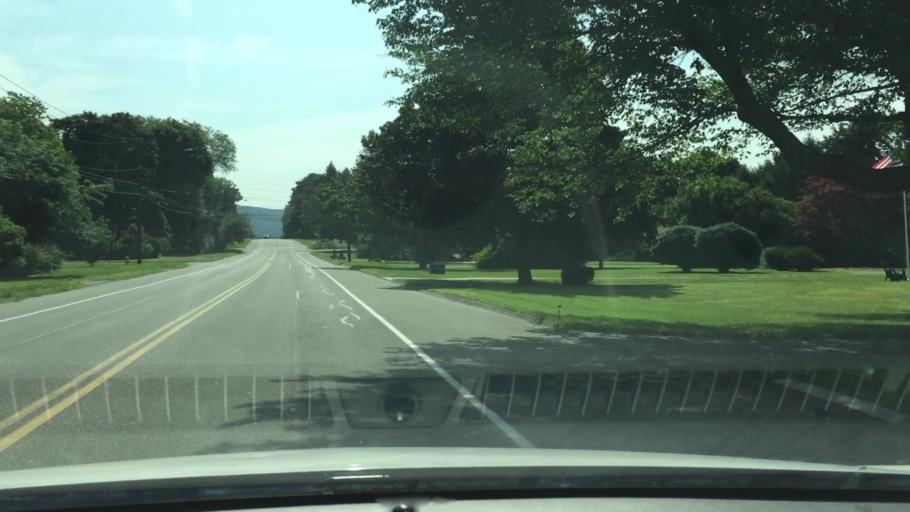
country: US
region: Massachusetts
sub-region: Berkshire County
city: Pittsfield
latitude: 42.4345
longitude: -73.2278
